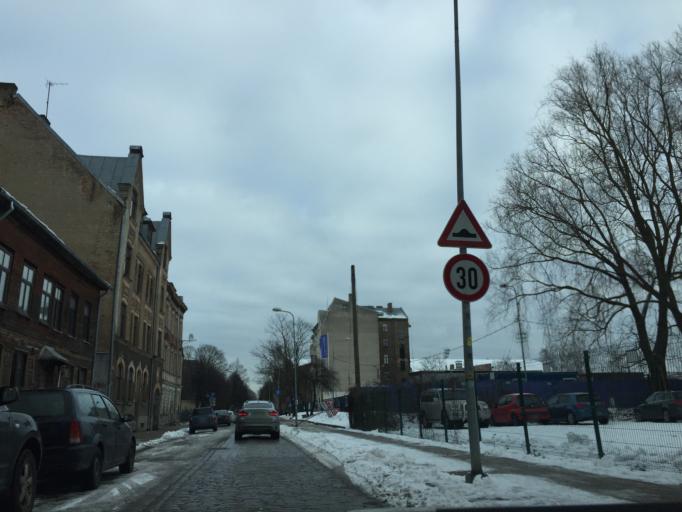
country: LV
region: Riga
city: Riga
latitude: 56.9606
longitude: 24.1101
